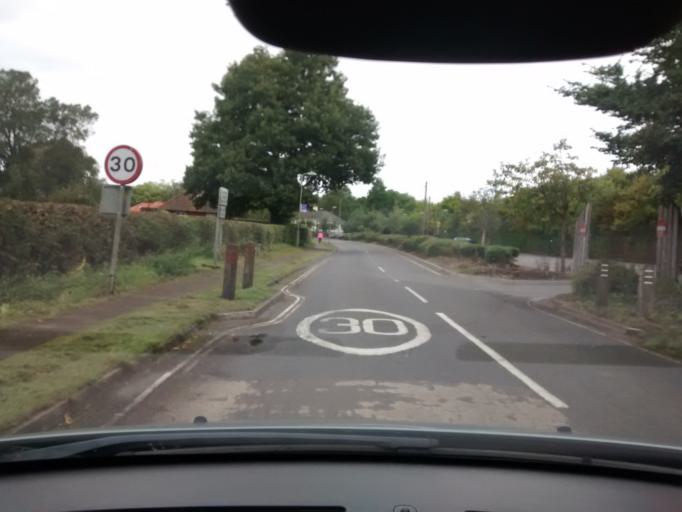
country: GB
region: England
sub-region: Hampshire
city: Fordingbridge
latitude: 50.9250
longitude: -1.7869
